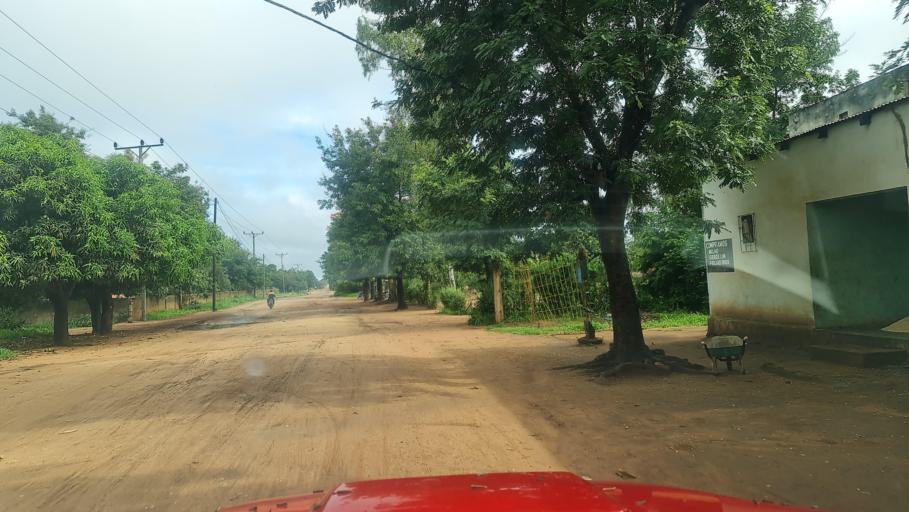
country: MW
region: Southern Region
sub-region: Nsanje District
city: Nsanje
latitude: -17.3206
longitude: 35.5919
